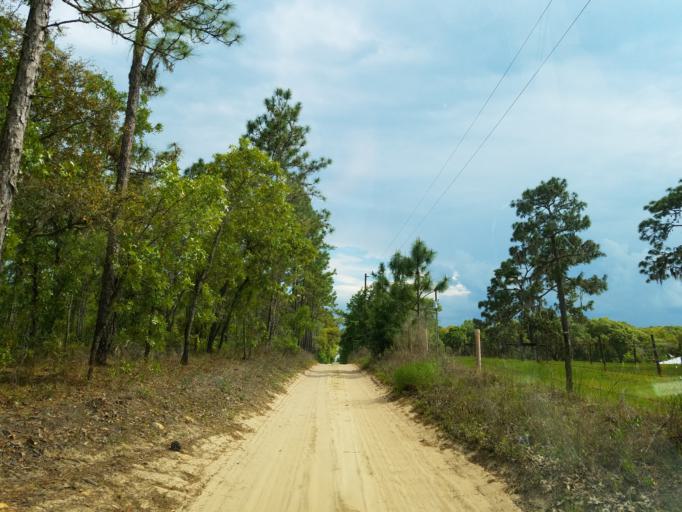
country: US
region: Florida
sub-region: Hernando County
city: Hill 'n Dale
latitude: 28.5476
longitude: -82.2760
